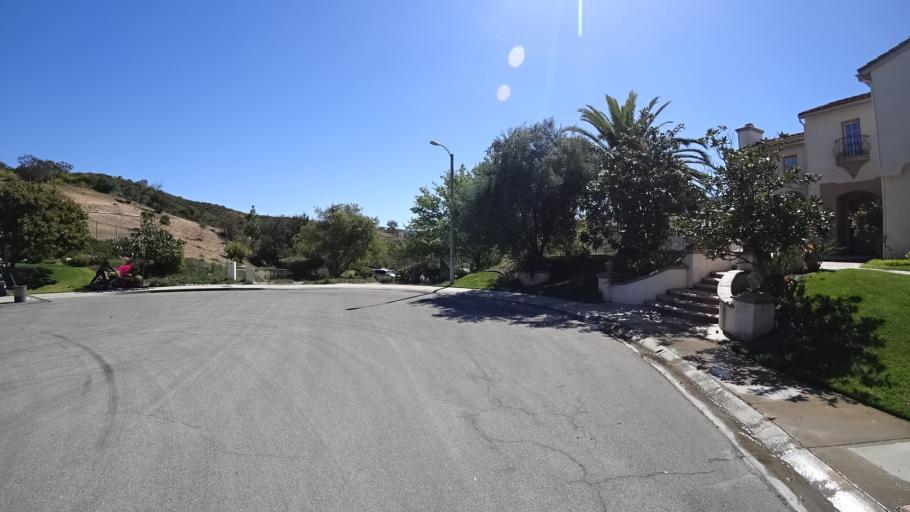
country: US
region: California
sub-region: Ventura County
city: Casa Conejo
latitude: 34.1613
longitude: -118.9687
